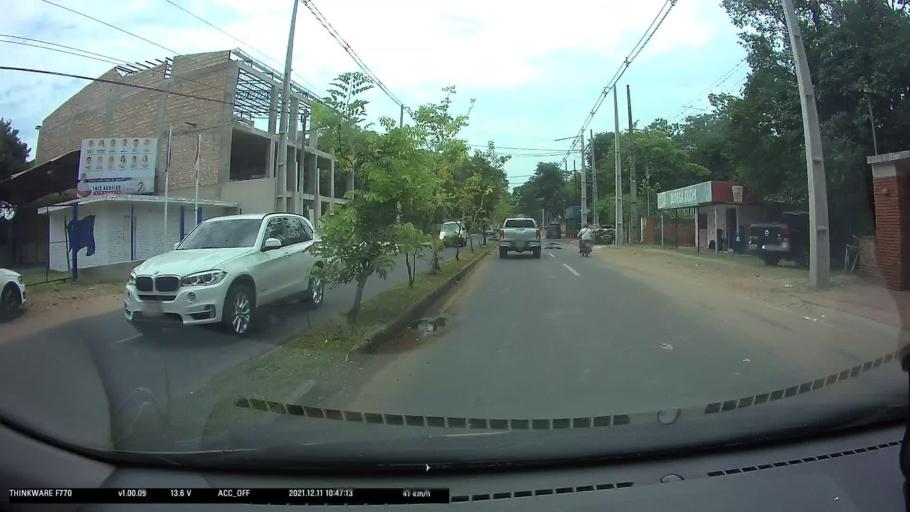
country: PY
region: Cordillera
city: San Bernardino
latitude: -25.3046
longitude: -57.2946
